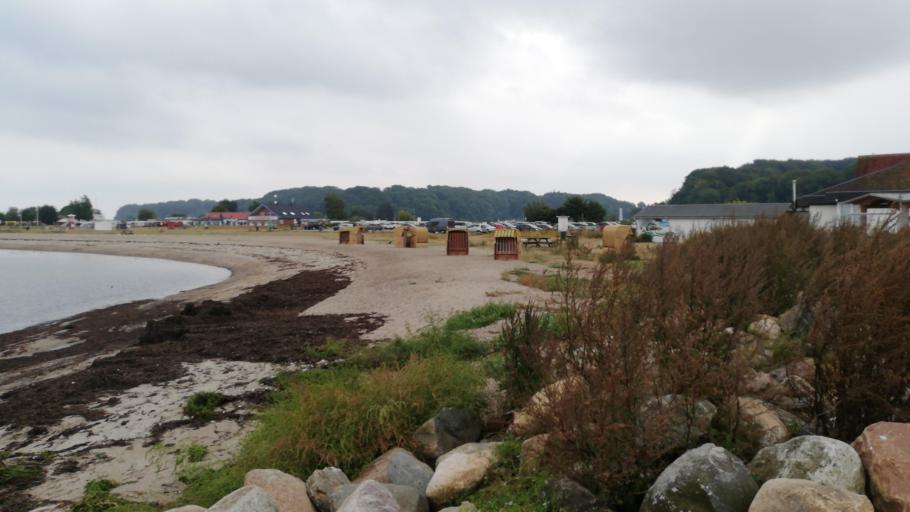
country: DE
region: Schleswig-Holstein
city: Westerholz
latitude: 54.8226
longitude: 9.6542
